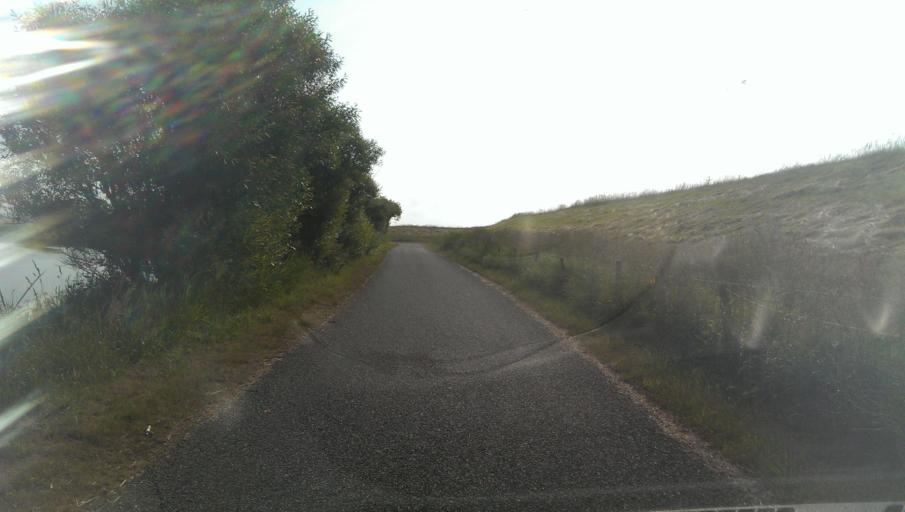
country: DK
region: South Denmark
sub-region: Esbjerg Kommune
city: Tjaereborg
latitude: 55.4331
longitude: 8.6106
